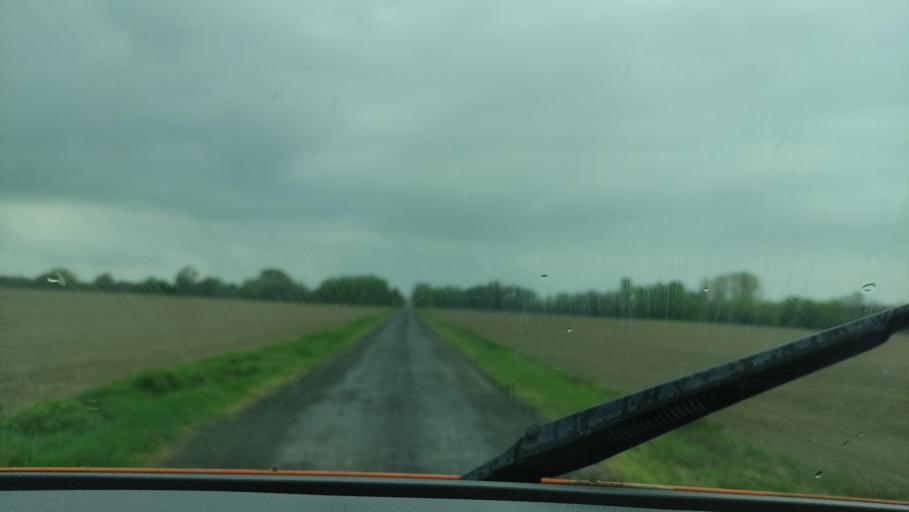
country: HR
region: Osjecko-Baranjska
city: Batina
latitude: 45.8962
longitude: 18.7877
